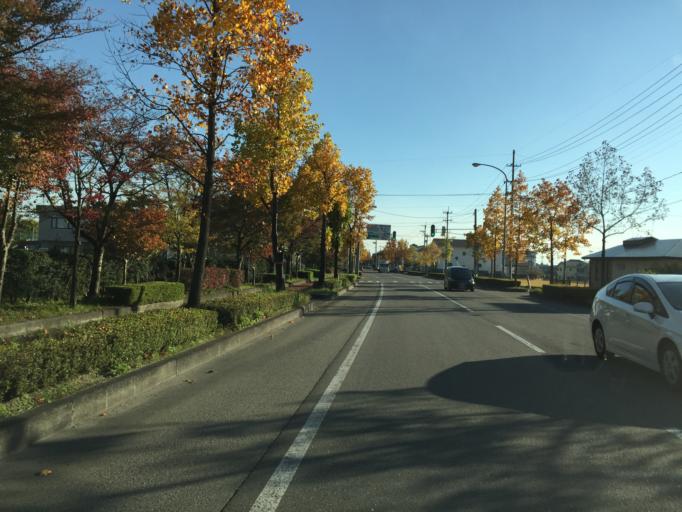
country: JP
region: Fukushima
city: Kitakata
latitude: 37.6582
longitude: 139.8862
